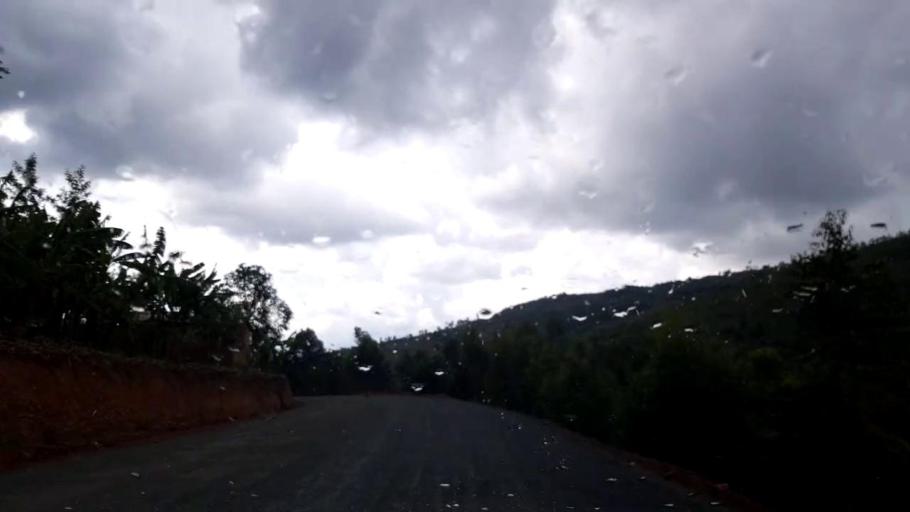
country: RW
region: Northern Province
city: Byumba
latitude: -1.6089
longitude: 30.2343
